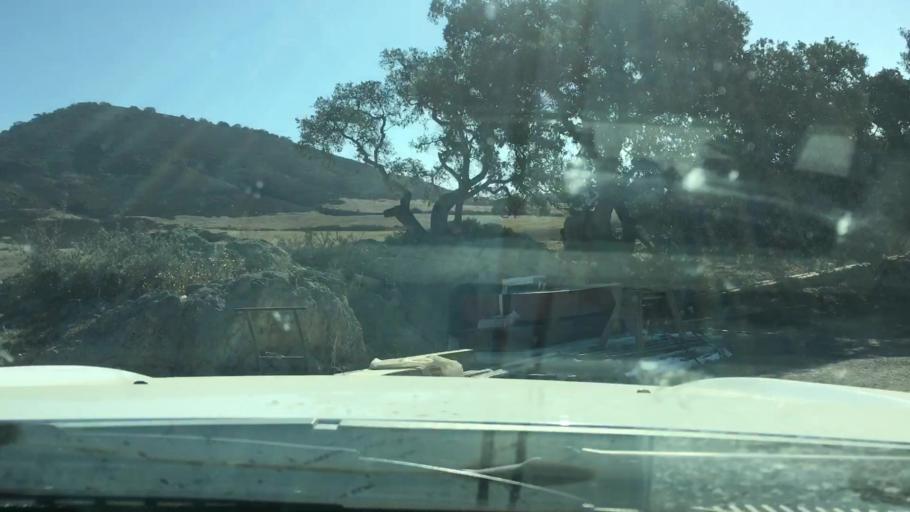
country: US
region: California
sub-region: San Luis Obispo County
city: Arroyo Grande
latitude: 35.1016
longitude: -120.5518
